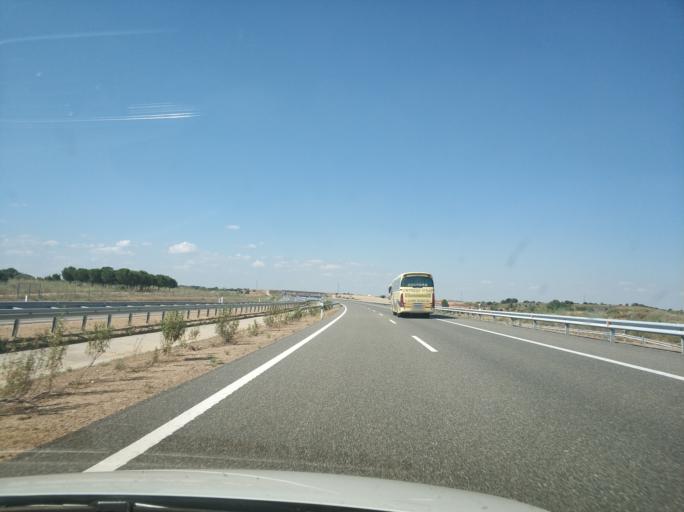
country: ES
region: Castille and Leon
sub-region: Provincia de Zamora
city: San Cebrian de Castro
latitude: 41.7009
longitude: -5.7926
